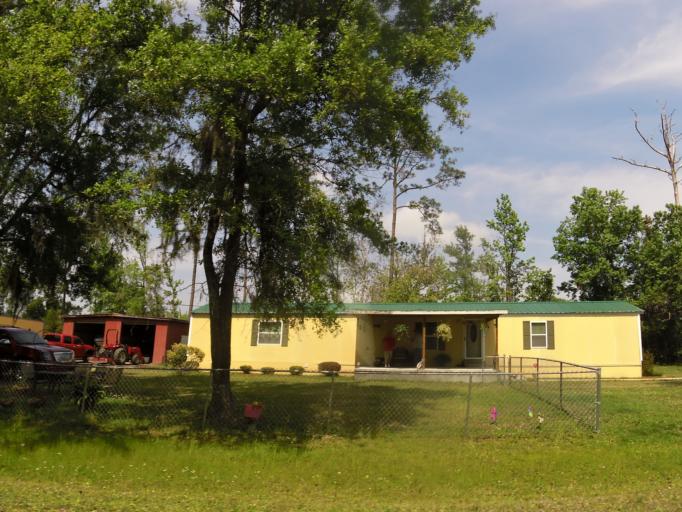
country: US
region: Georgia
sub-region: Camden County
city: Kingsland
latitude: 30.7908
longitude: -81.7162
